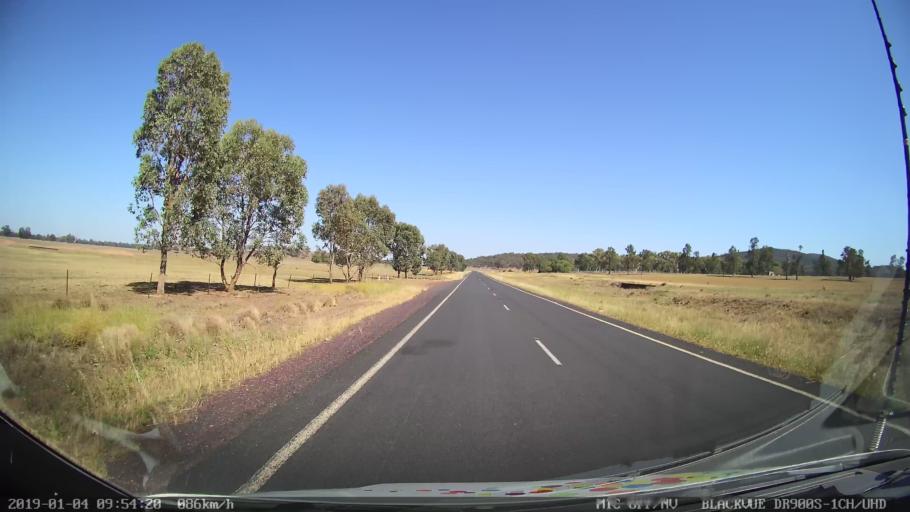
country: AU
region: New South Wales
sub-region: Cabonne
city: Canowindra
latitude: -33.5422
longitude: 148.4159
